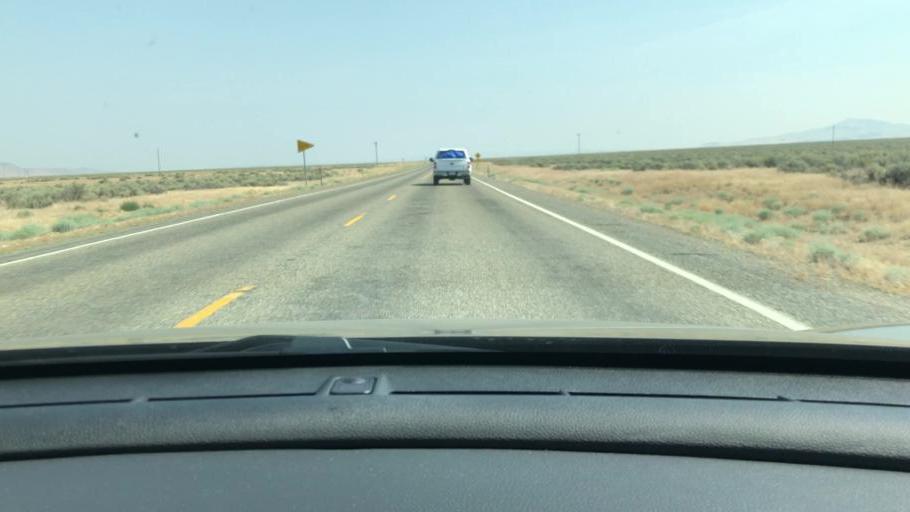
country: US
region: Nevada
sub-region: Humboldt County
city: Winnemucca
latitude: 41.7261
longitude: -117.7675
